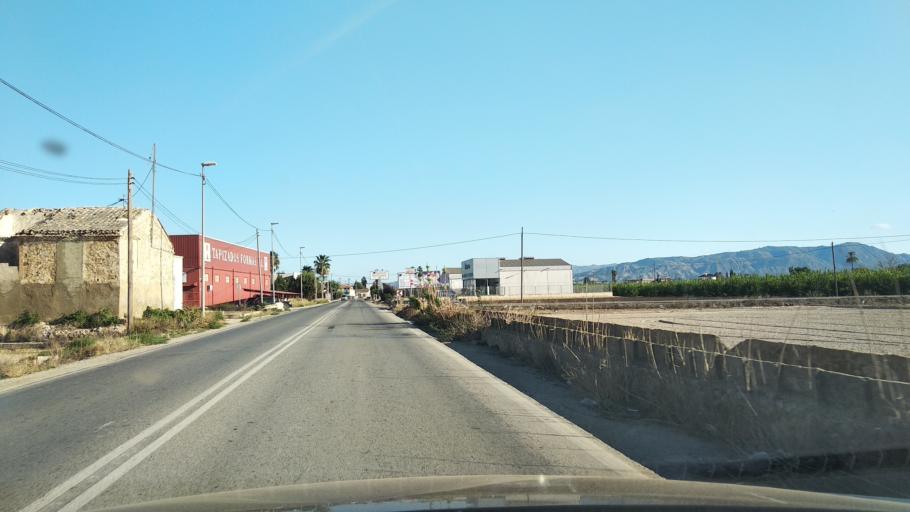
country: ES
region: Murcia
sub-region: Murcia
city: Santomera
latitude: 38.0437
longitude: -1.0517
